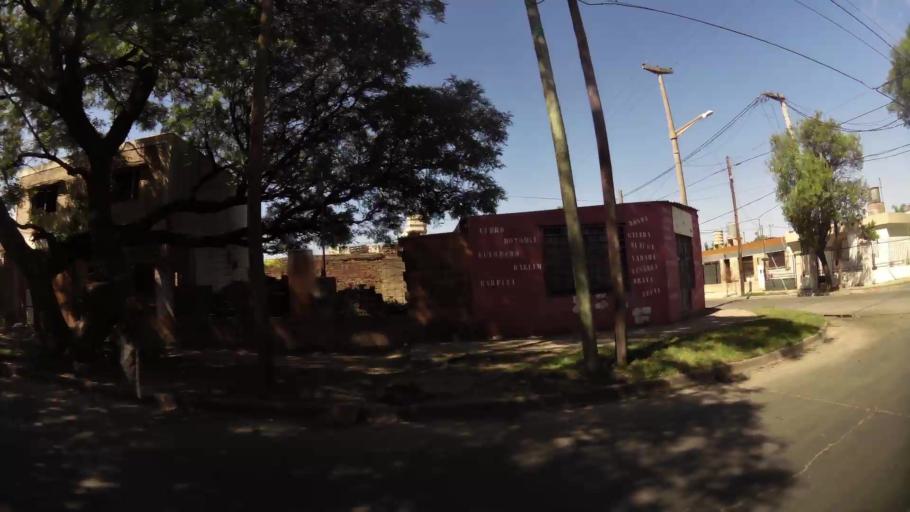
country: AR
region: Cordoba
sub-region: Departamento de Capital
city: Cordoba
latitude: -31.3688
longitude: -64.1674
